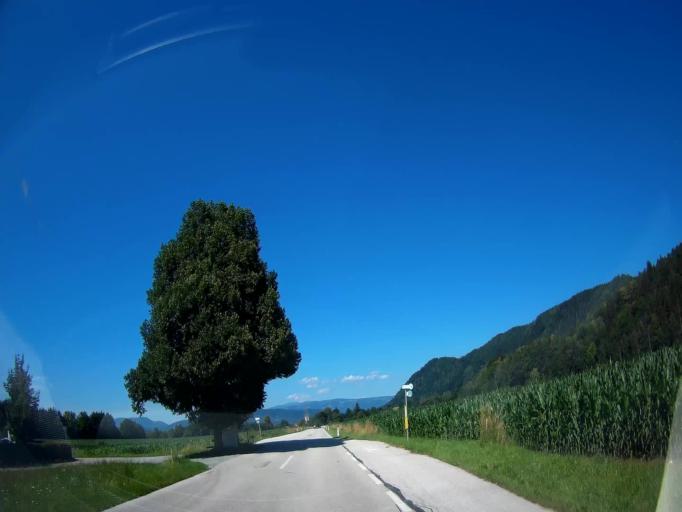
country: AT
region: Carinthia
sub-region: Politischer Bezirk Volkermarkt
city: Gallizien
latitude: 46.5803
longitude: 14.5110
